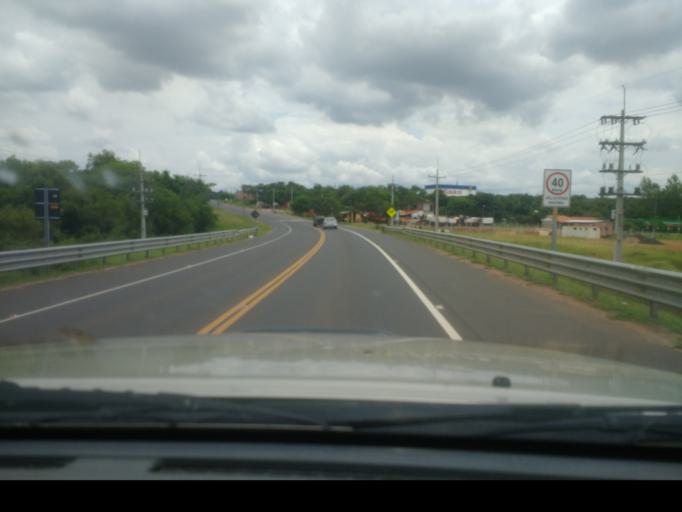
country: PY
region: Central
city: Limpio
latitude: -25.1308
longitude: -57.4463
